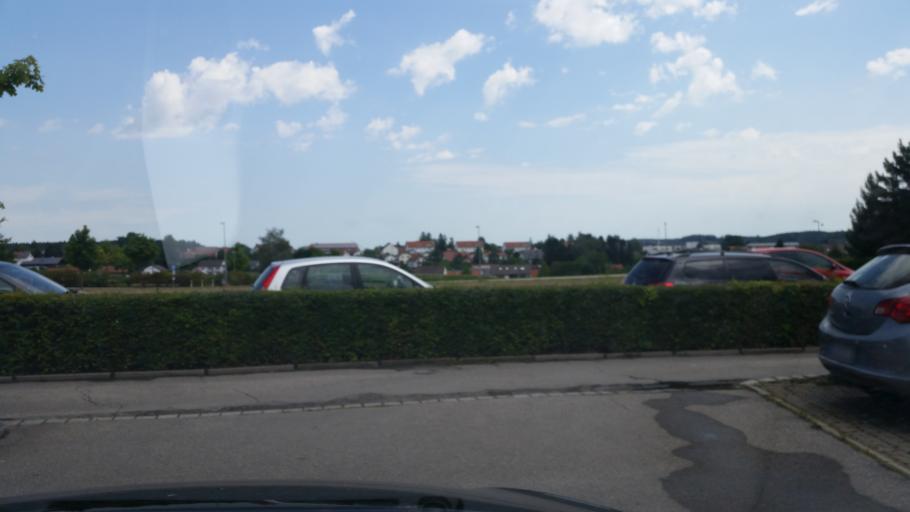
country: DE
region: Bavaria
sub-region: Lower Bavaria
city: Vilsbiburg
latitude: 48.4530
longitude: 12.3457
